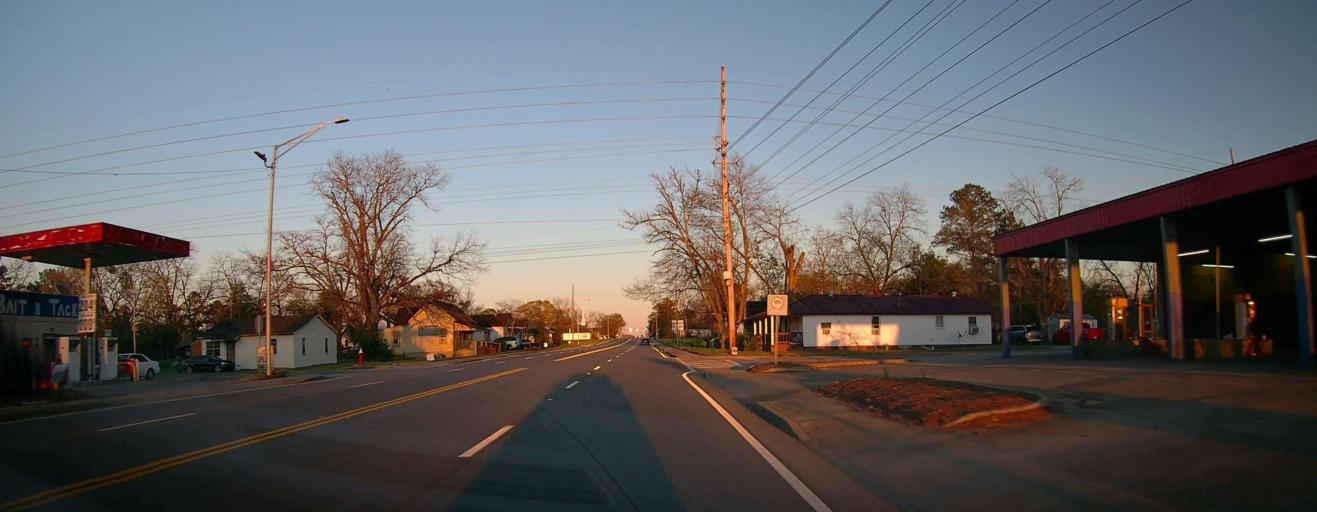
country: US
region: Georgia
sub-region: Crisp County
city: Cordele
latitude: 31.9634
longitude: -83.7946
